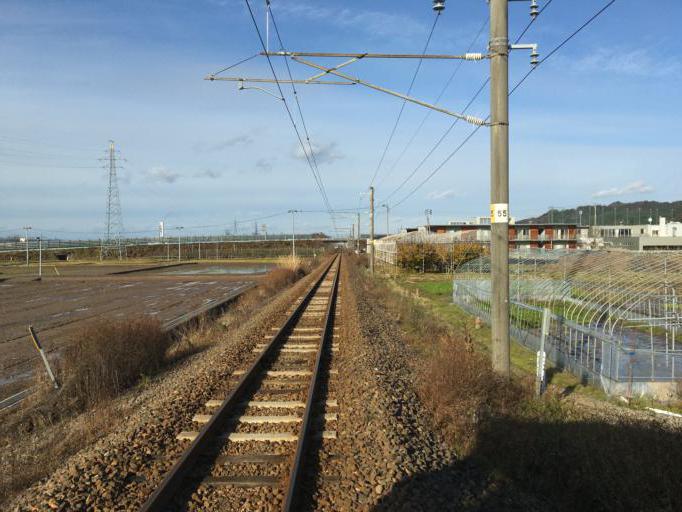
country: JP
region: Akita
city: Yuzawa
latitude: 39.1379
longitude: 140.4855
